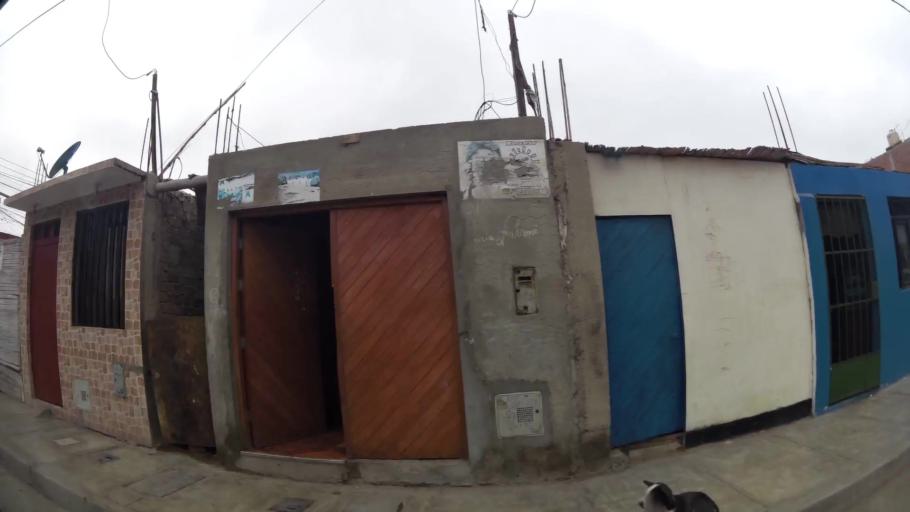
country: PE
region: Ica
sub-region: Provincia de Pisco
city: Pisco
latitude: -13.7307
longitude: -76.2217
